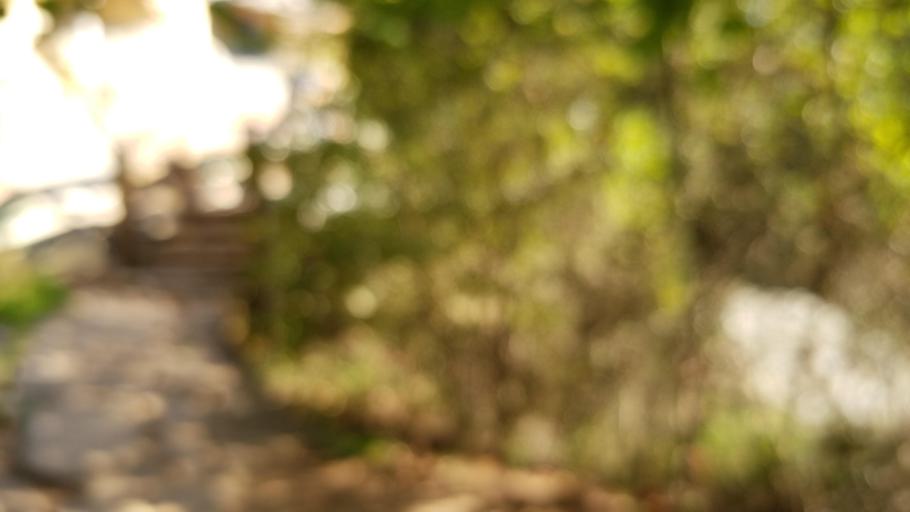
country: US
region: Illinois
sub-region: Hardin County
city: Elizabethtown
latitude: 37.6047
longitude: -88.3858
